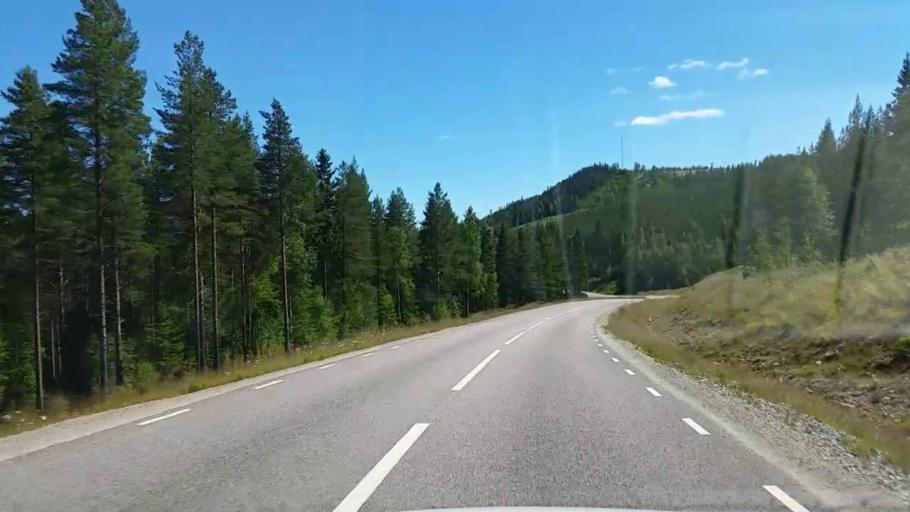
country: SE
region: Gaevleborg
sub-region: Ovanakers Kommun
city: Edsbyn
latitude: 61.5874
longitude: 15.6384
